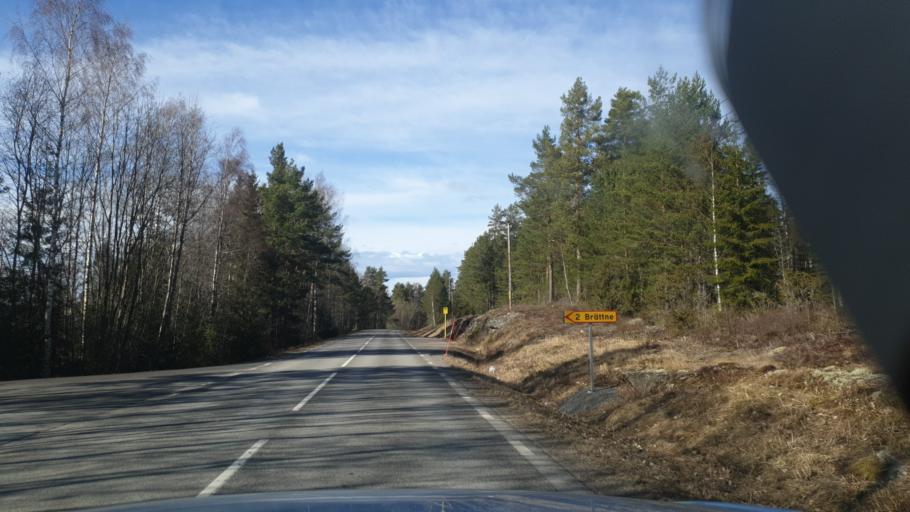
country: SE
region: Vaermland
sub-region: Arvika Kommun
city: Arvika
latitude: 59.7312
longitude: 12.5636
